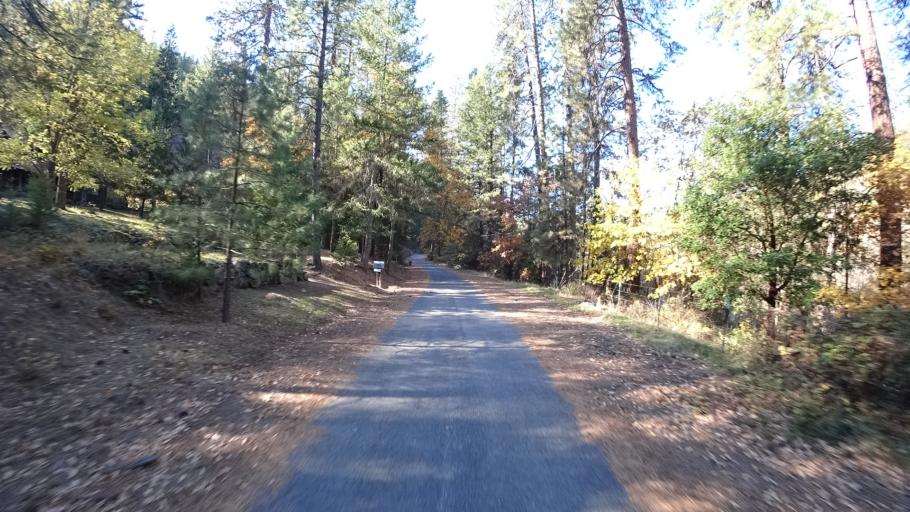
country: US
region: California
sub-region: Siskiyou County
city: Yreka
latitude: 41.8316
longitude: -122.9495
